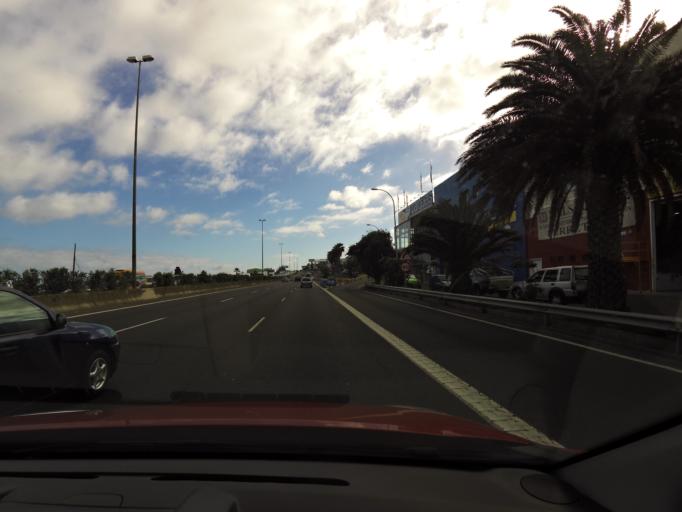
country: ES
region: Canary Islands
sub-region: Provincia de Las Palmas
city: Telde
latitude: 27.9690
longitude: -15.3907
